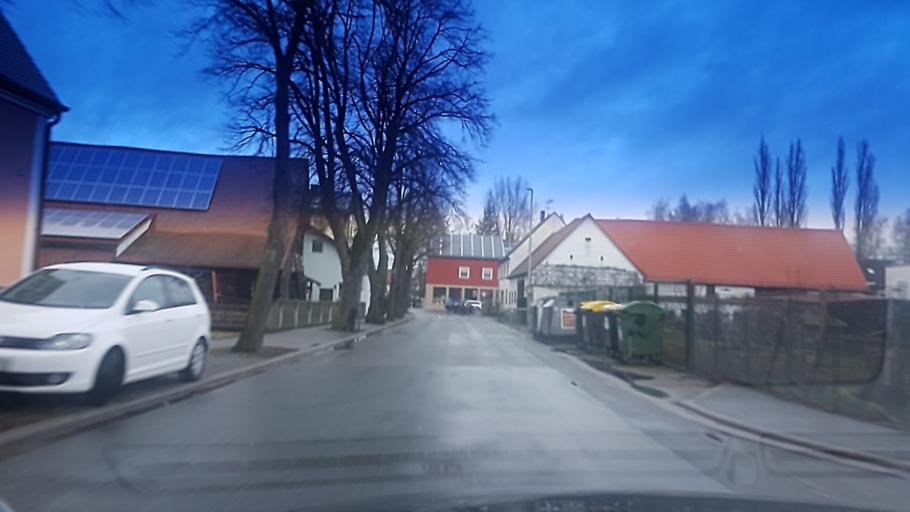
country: DE
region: Bavaria
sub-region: Upper Franconia
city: Burgebrach
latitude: 49.8262
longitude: 10.7453
